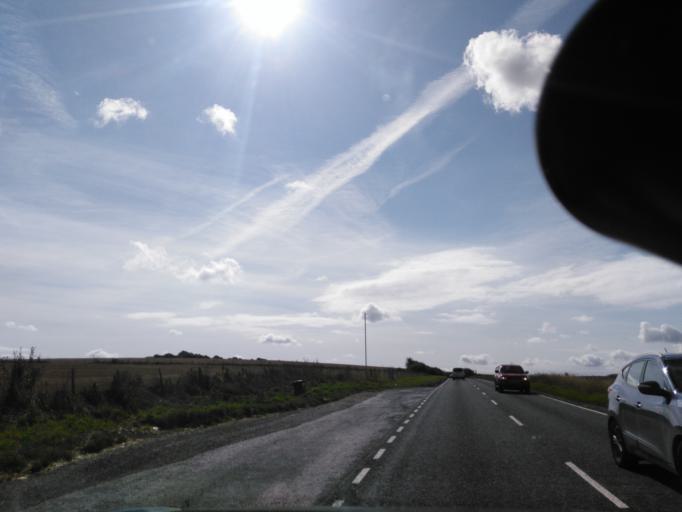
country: GB
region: England
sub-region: Wiltshire
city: Bishopstrow
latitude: 51.1494
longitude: -2.1645
